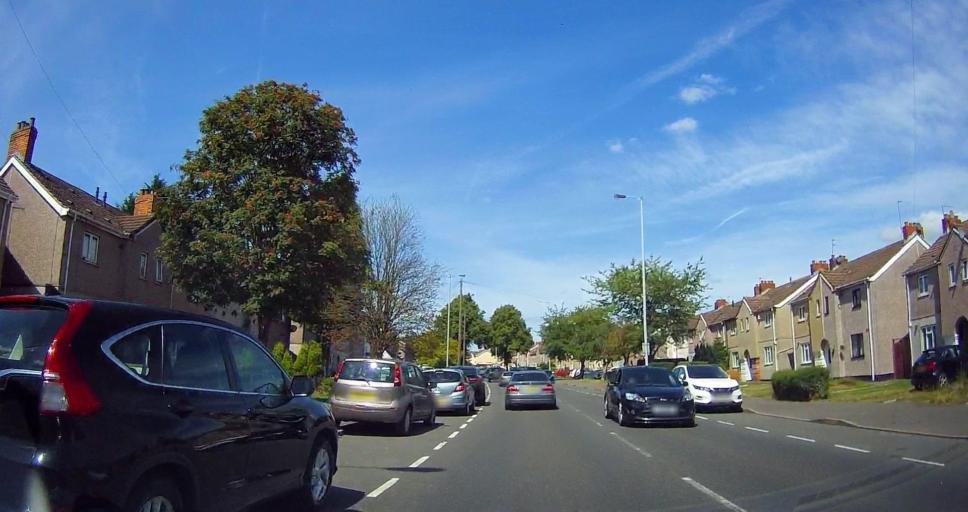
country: GB
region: England
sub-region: Wolverhampton
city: Wolverhampton
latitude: 52.5701
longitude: -2.1183
